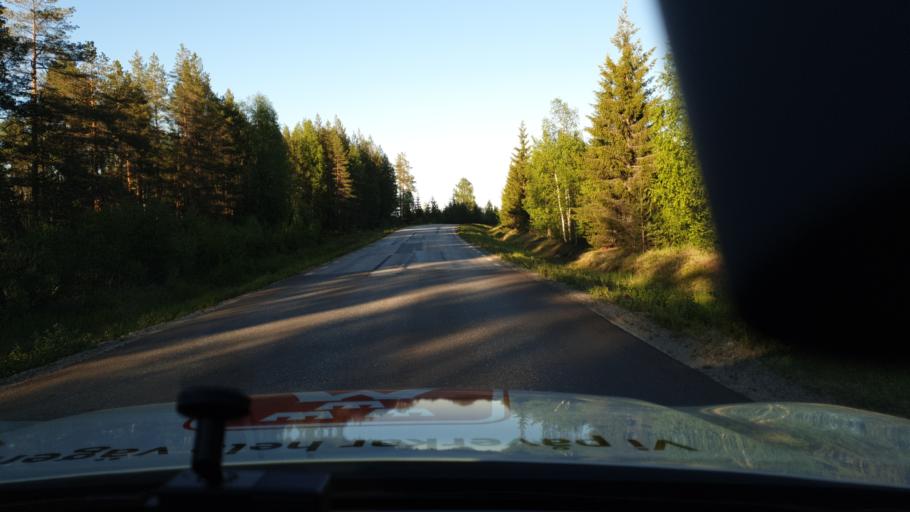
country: SE
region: Vaesterbotten
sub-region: Umea Kommun
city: Ersmark
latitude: 64.0110
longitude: 20.1804
